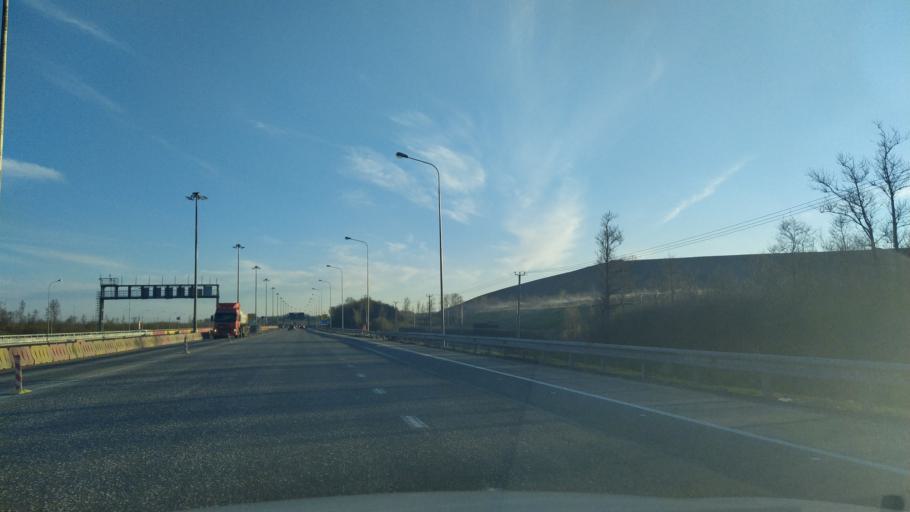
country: RU
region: St.-Petersburg
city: Levashovo
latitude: 60.0745
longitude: 30.1796
